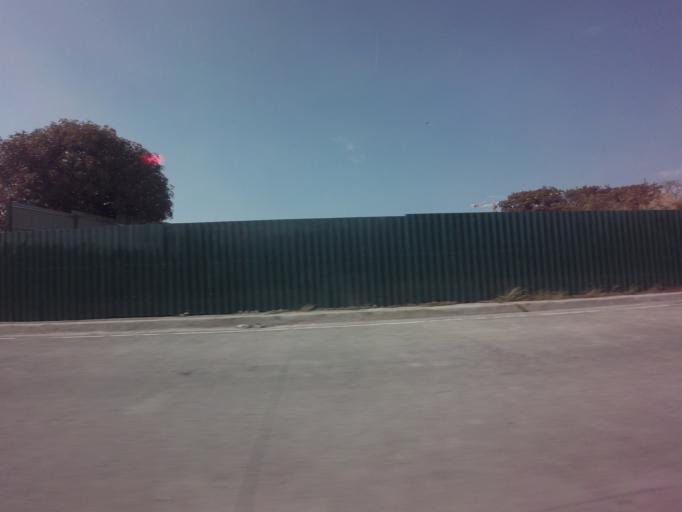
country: PH
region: Calabarzon
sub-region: Province of Rizal
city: Taguig
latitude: 14.5036
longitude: 121.0415
